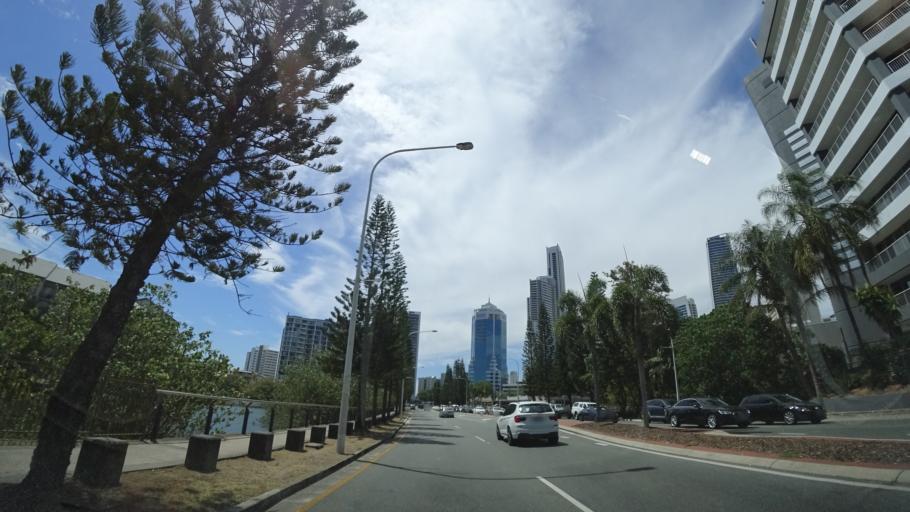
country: AU
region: Queensland
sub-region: Gold Coast
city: Surfers Paradise
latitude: -28.0054
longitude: 153.4279
